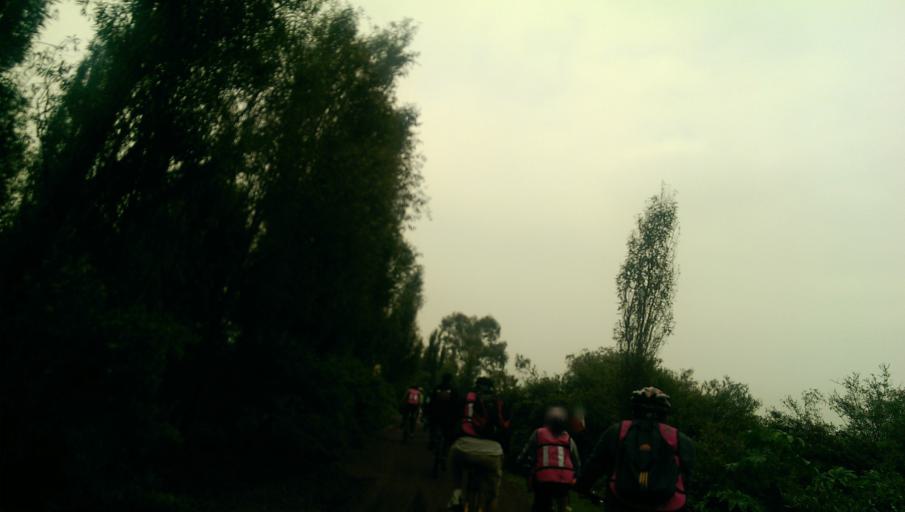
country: MX
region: Mexico City
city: Xochimilco
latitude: 19.2681
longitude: -99.0702
